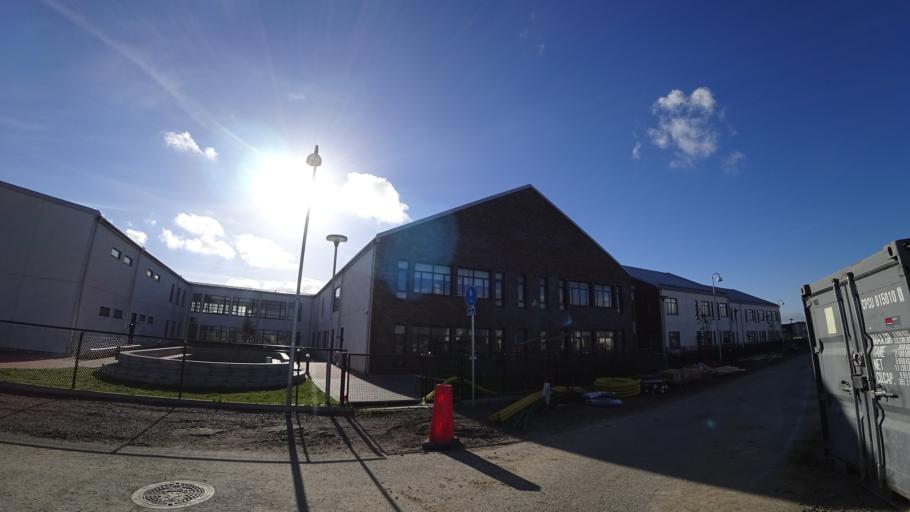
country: SE
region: Skane
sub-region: Staffanstorps Kommun
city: Hjaerup
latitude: 55.6705
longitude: 13.1564
